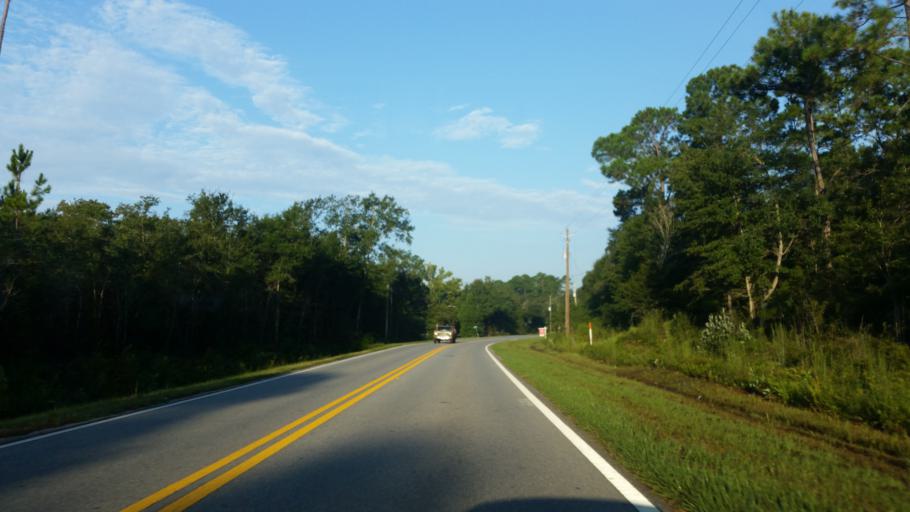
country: US
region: Florida
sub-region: Santa Rosa County
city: East Milton
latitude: 30.6073
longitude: -87.0158
